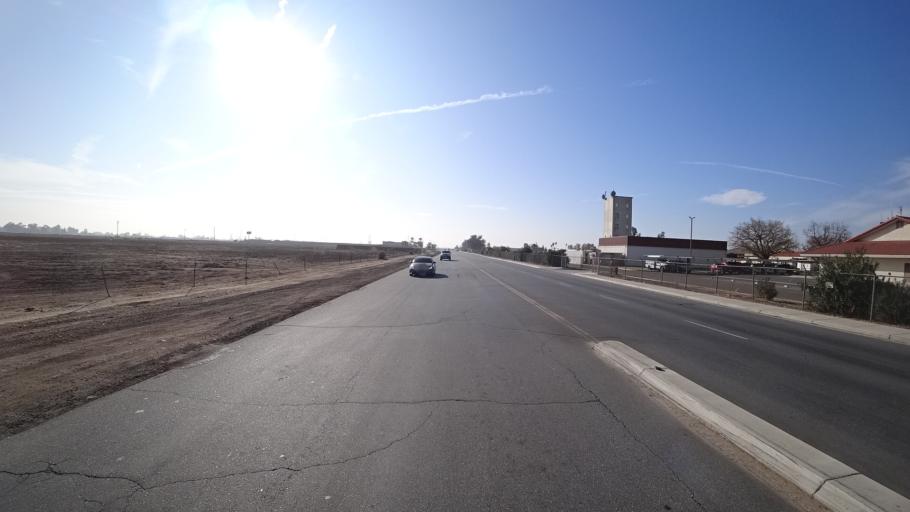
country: US
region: California
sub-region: Kern County
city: Oildale
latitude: 35.4111
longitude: -119.0587
